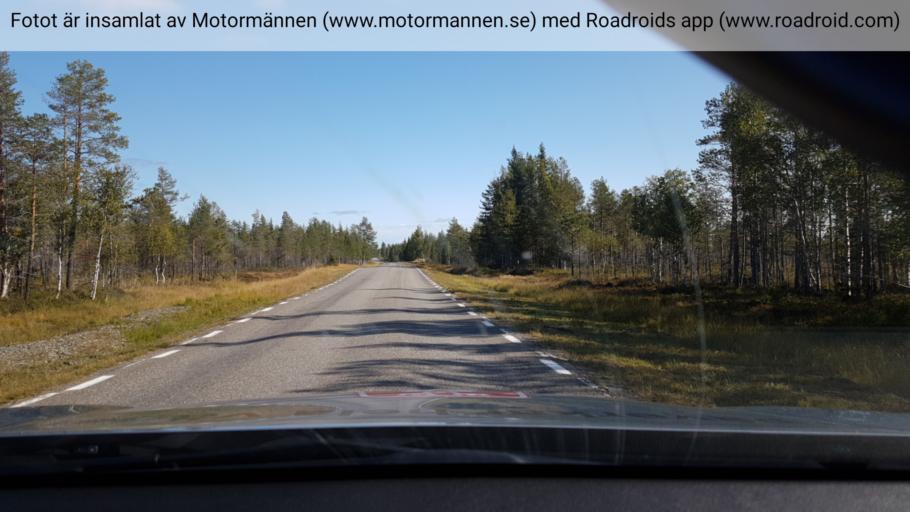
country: SE
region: Vaesterbotten
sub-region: Norsjo Kommun
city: Norsjoe
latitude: 65.1302
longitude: 19.2386
